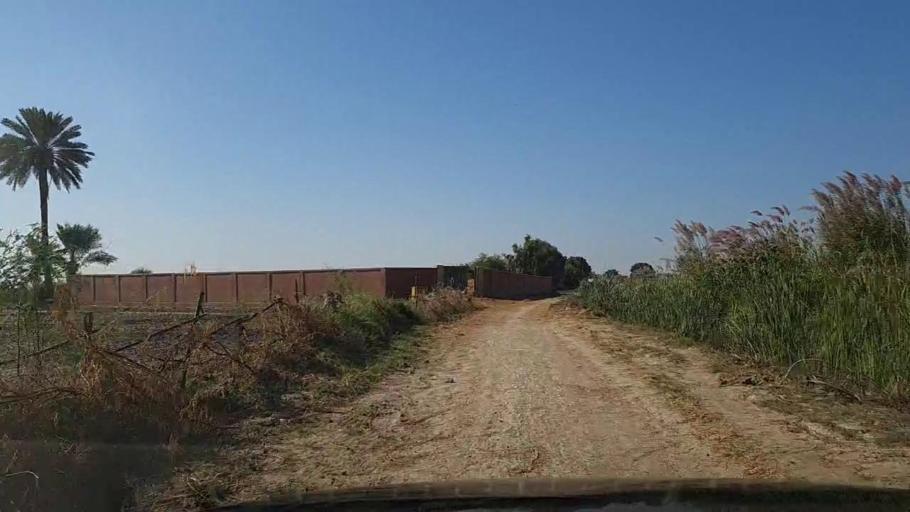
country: PK
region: Sindh
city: Thatta
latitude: 24.7037
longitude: 67.9078
